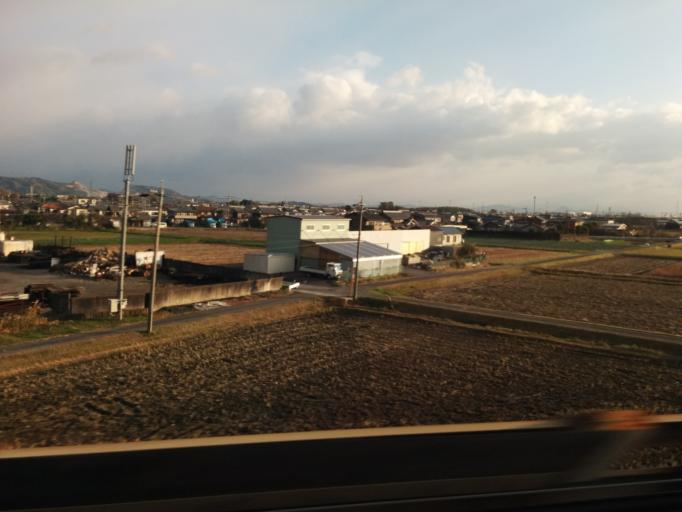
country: JP
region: Gifu
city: Tarui
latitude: 35.3548
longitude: 136.5463
